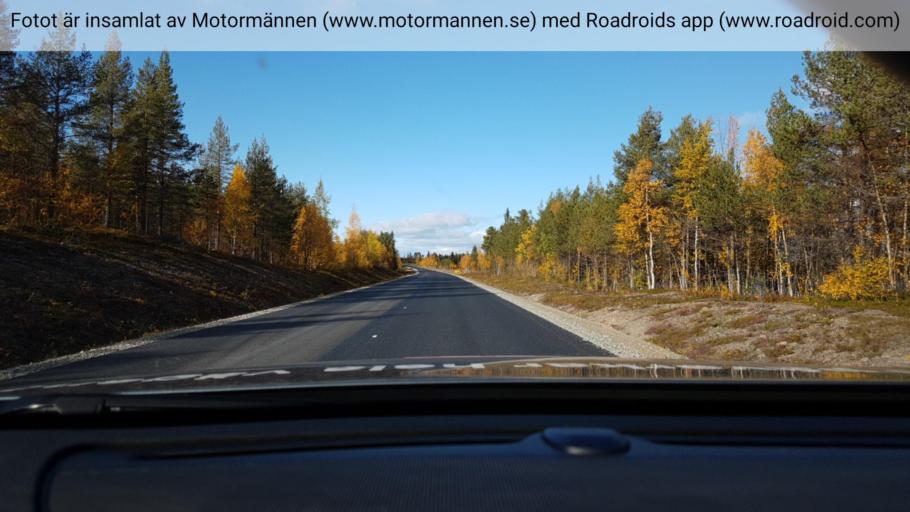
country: SE
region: Norrbotten
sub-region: Arjeplogs Kommun
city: Arjeplog
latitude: 65.9742
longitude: 18.2421
